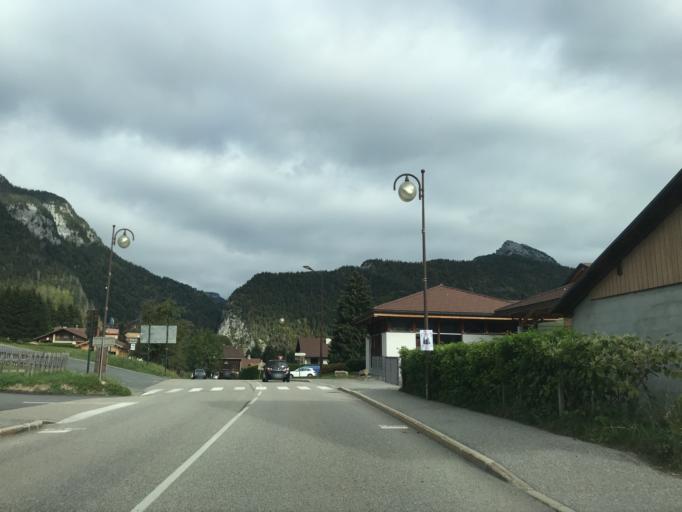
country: FR
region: Rhone-Alpes
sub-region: Departement de la Haute-Savoie
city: Saint-Jean-de-Sixt
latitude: 45.9234
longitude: 6.4101
